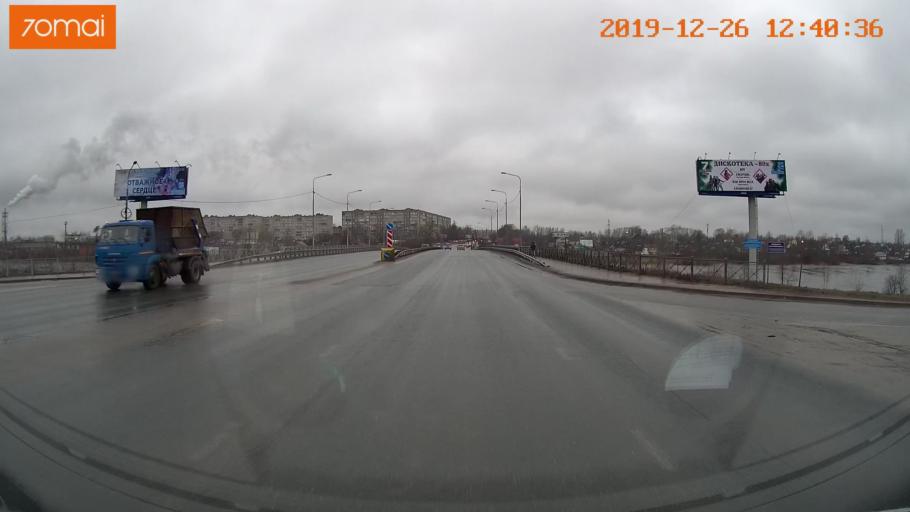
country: RU
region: Vologda
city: Tonshalovo
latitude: 59.1426
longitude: 37.9706
